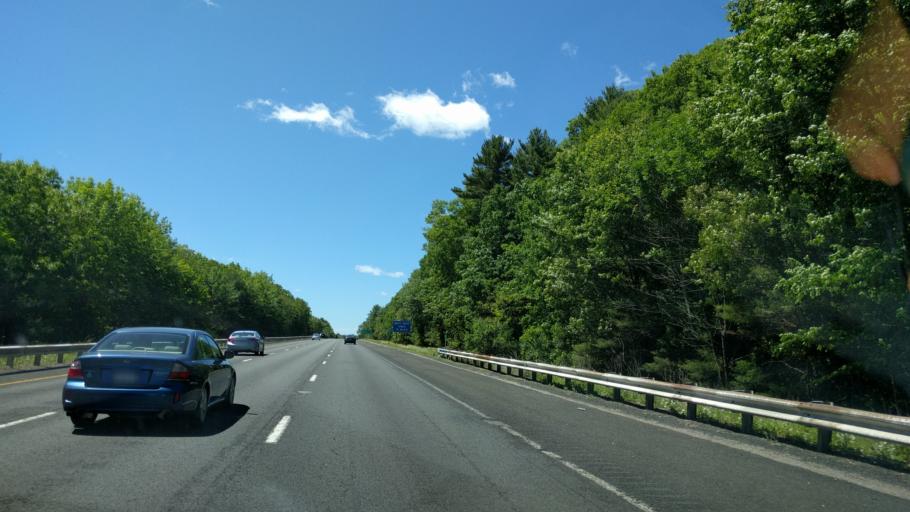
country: US
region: Massachusetts
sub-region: Hampden County
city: Holland
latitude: 42.0617
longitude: -72.1128
